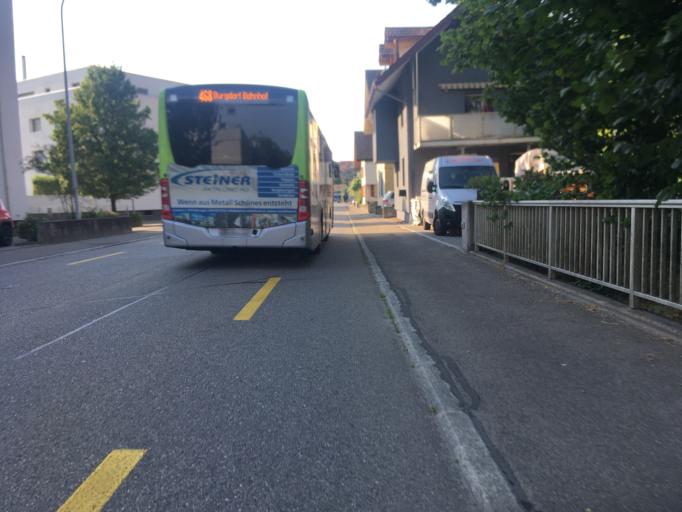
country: CH
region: Bern
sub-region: Emmental District
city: Burgdorf
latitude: 47.0513
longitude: 7.6303
